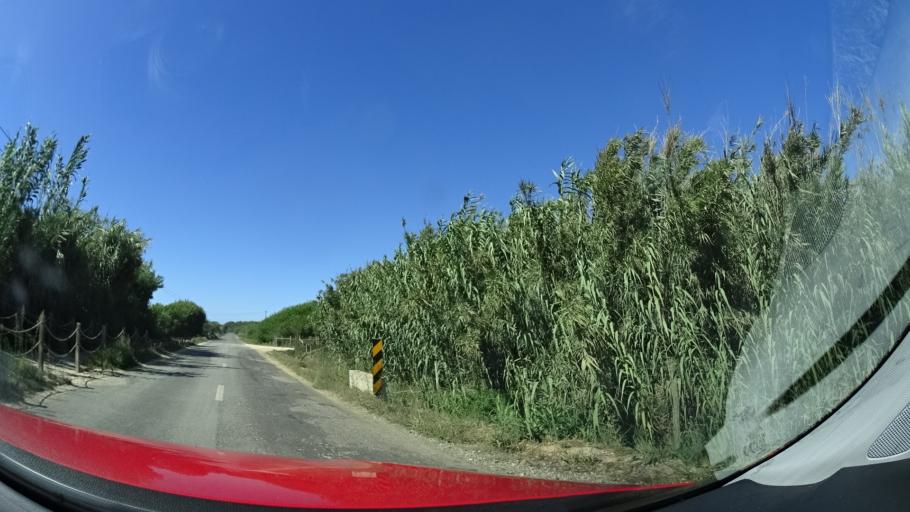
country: PT
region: Beja
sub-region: Odemira
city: Sao Teotonio
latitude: 37.5435
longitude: -8.7880
